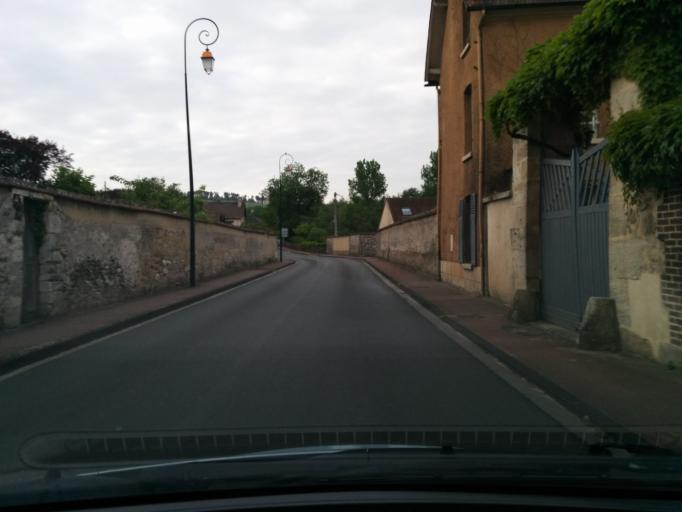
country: FR
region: Haute-Normandie
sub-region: Departement de l'Eure
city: Gasny
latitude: 49.0876
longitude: 1.6084
